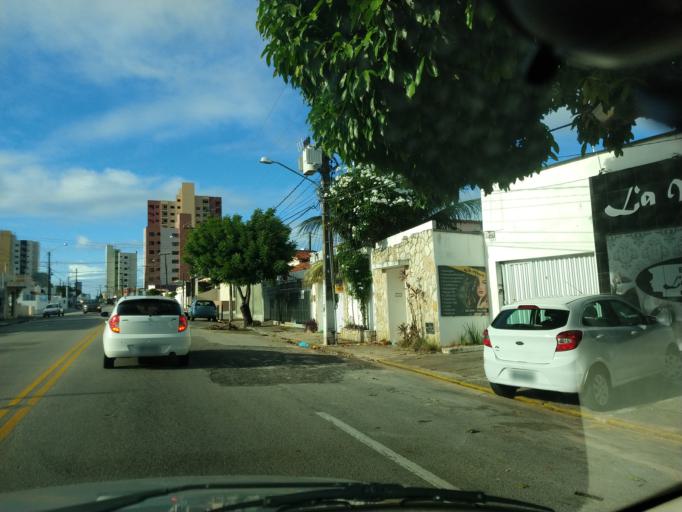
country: BR
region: Rio Grande do Norte
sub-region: Natal
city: Natal
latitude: -5.7984
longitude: -35.2107
